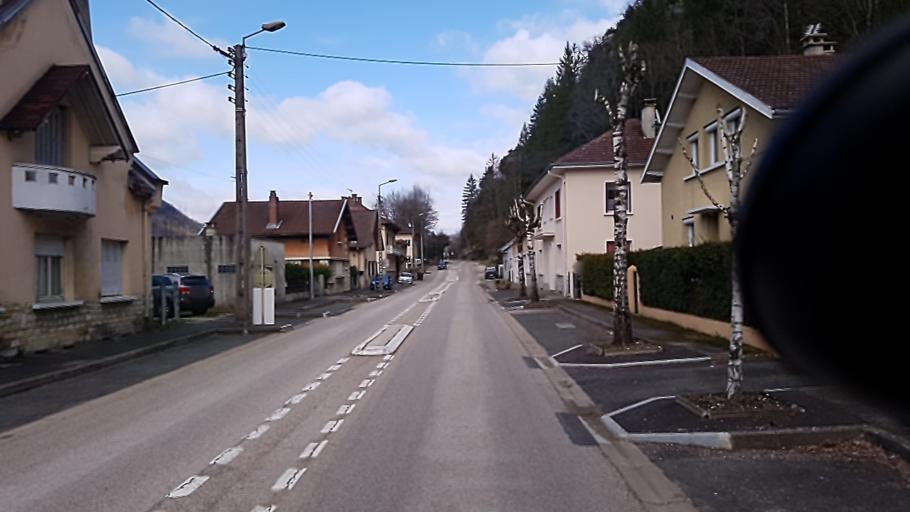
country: FR
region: Rhone-Alpes
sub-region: Departement de l'Ain
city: Dortan
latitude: 46.3194
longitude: 5.6608
